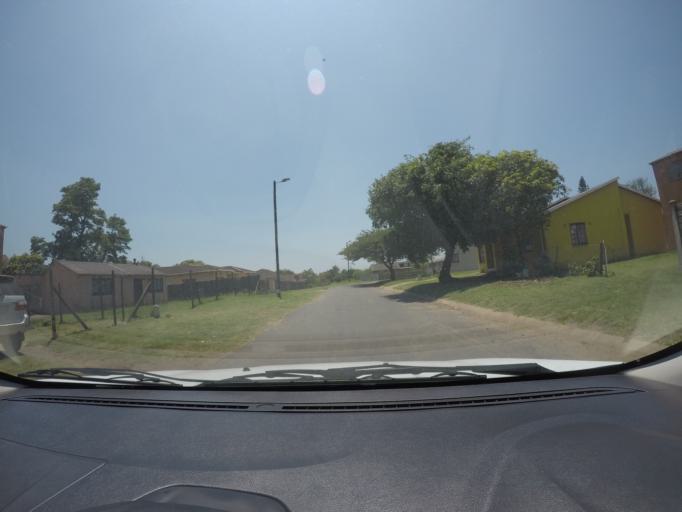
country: ZA
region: KwaZulu-Natal
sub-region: uThungulu District Municipality
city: eSikhawini
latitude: -28.8708
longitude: 31.9085
